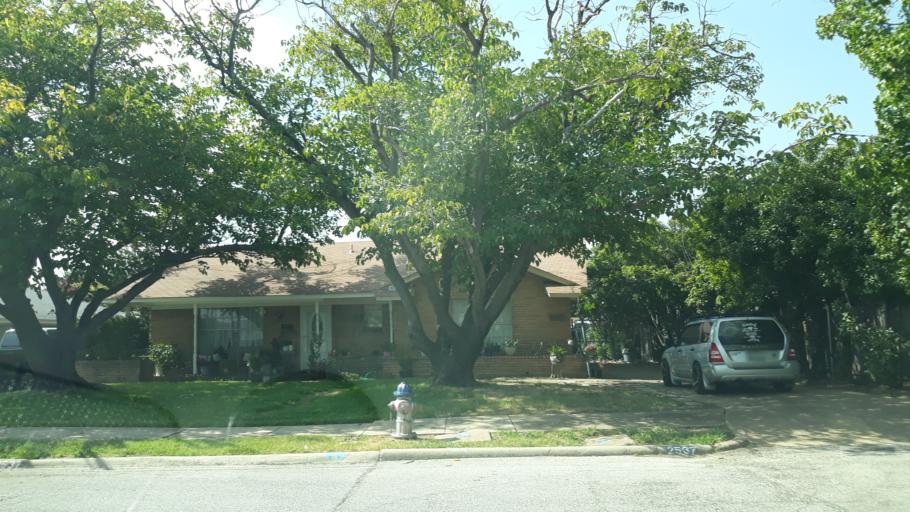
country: US
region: Texas
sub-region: Dallas County
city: Irving
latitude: 32.8414
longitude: -96.9965
